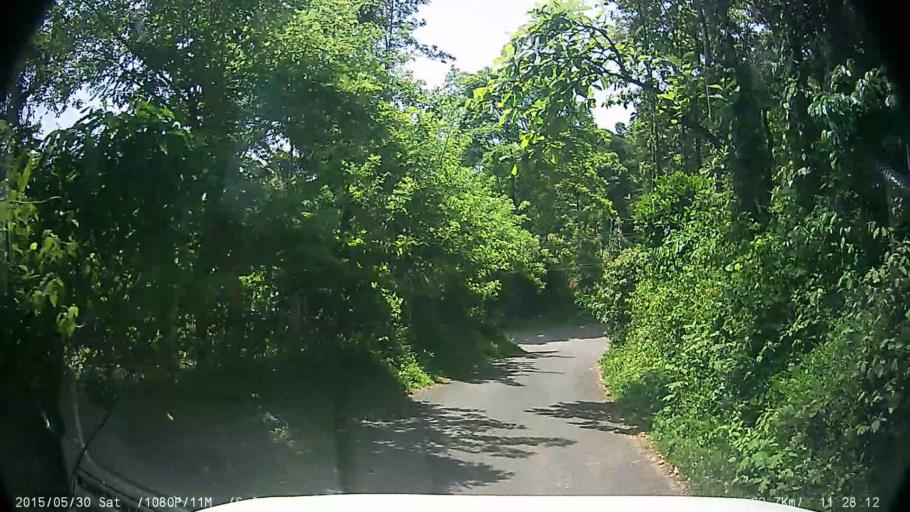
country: IN
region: Kerala
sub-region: Wayanad
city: Panamaram
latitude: 11.8121
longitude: 76.0444
